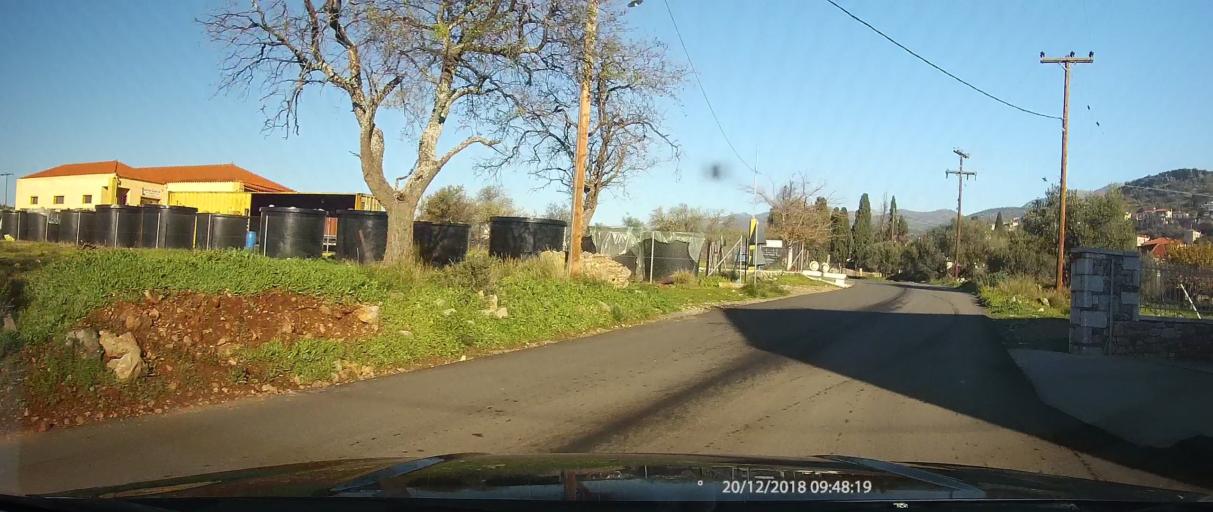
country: GR
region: Peloponnese
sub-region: Nomos Lakonias
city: Yerakion
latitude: 36.9900
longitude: 22.7021
